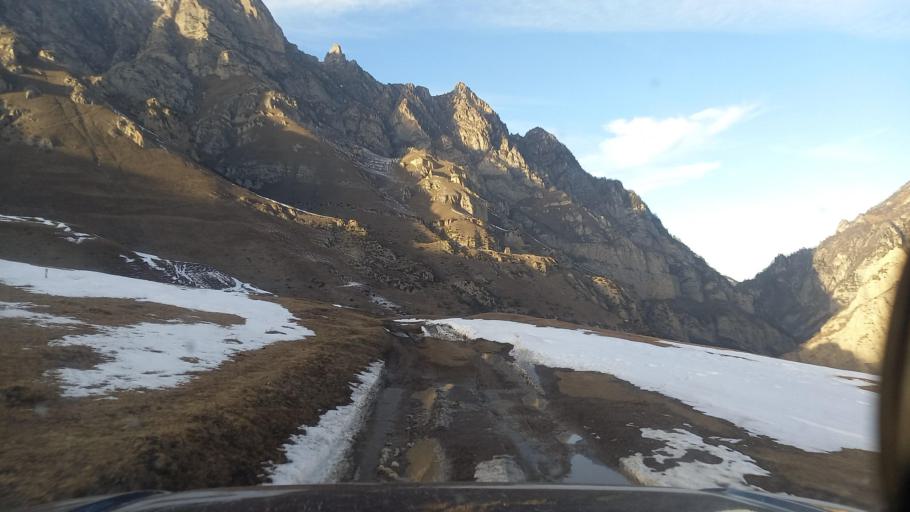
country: RU
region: Ingushetiya
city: Dzhayrakh
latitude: 42.8555
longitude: 44.5157
